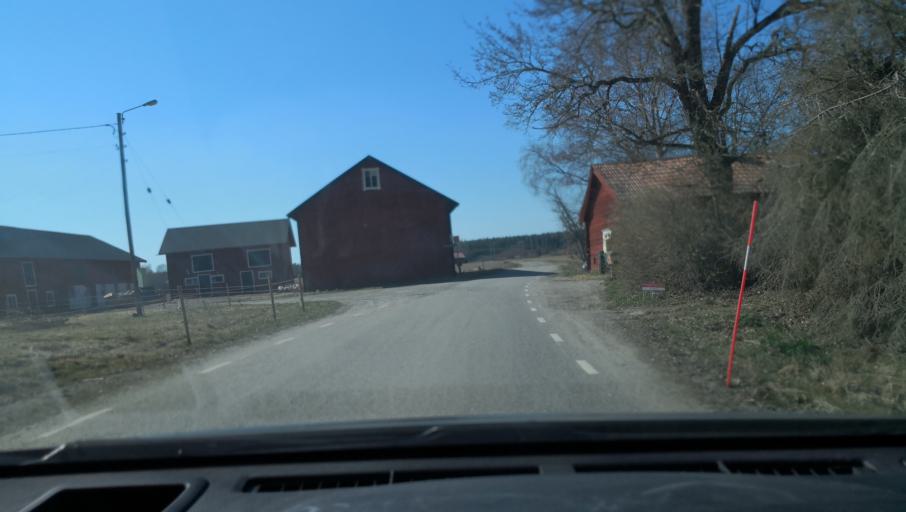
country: SE
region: Vaestmanland
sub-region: Sala Kommun
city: Sala
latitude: 59.8767
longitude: 16.5374
